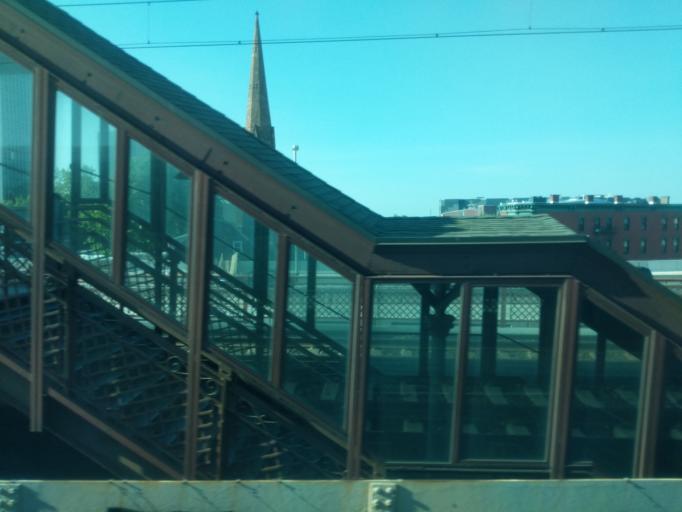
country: US
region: New Jersey
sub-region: Hudson County
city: East Newark
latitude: 40.7475
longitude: -74.1709
